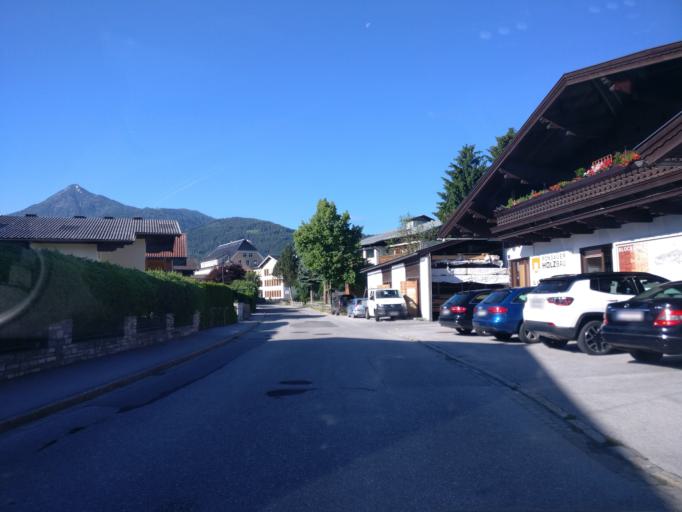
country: AT
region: Salzburg
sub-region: Politischer Bezirk Sankt Johann im Pongau
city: Altenmarkt im Pongau
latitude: 47.3794
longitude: 13.4275
